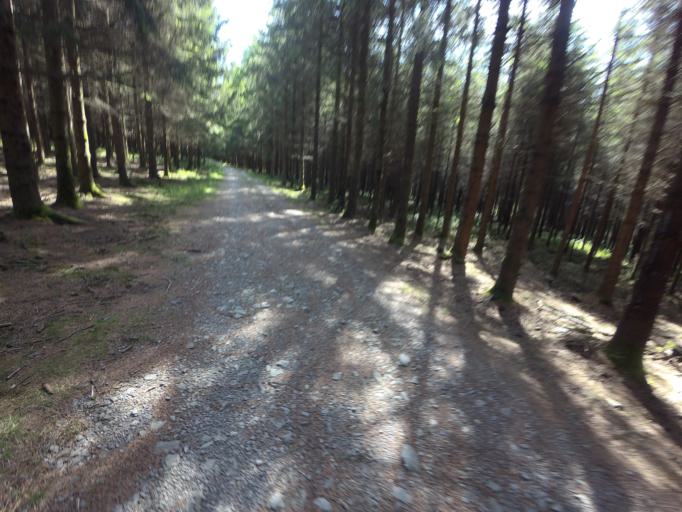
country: BE
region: Wallonia
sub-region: Province de Liege
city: Malmedy
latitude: 50.4914
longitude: 6.0046
